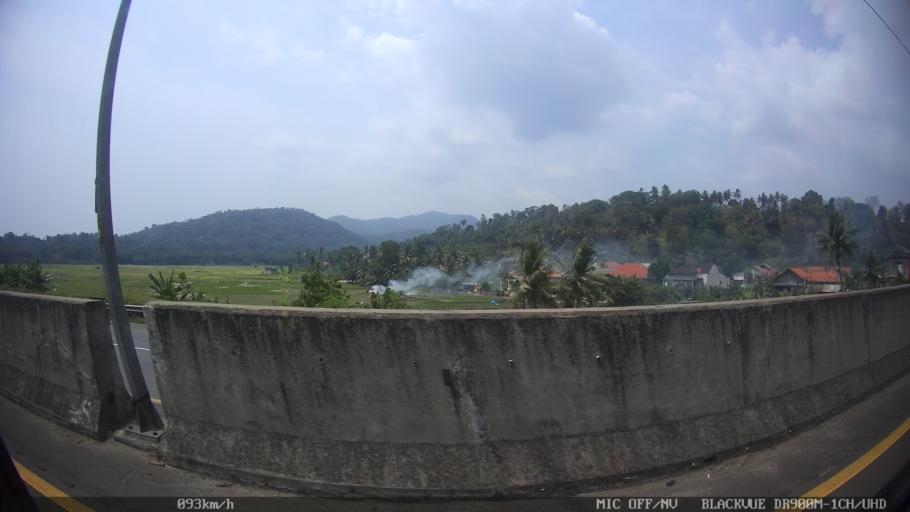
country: ID
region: Banten
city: Curug
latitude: -5.9780
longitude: 106.0127
